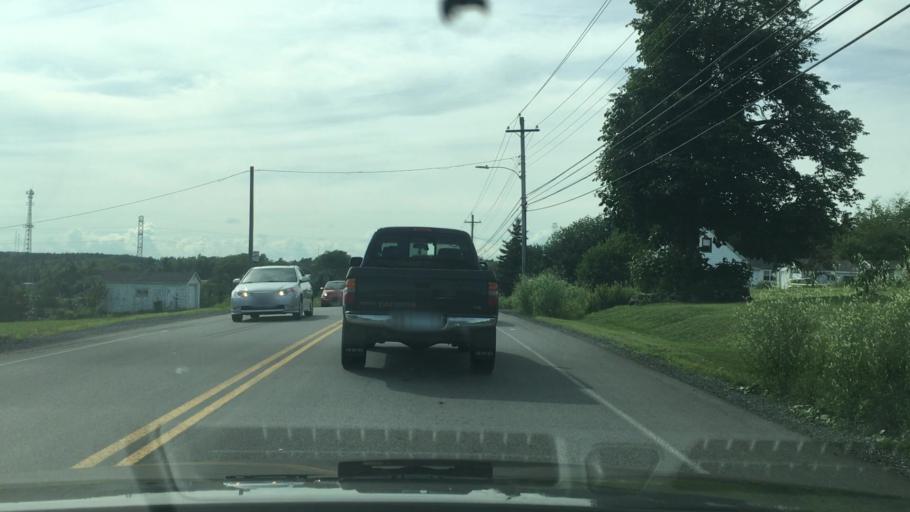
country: CA
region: Nova Scotia
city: Dartmouth
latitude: 44.7308
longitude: -63.7542
